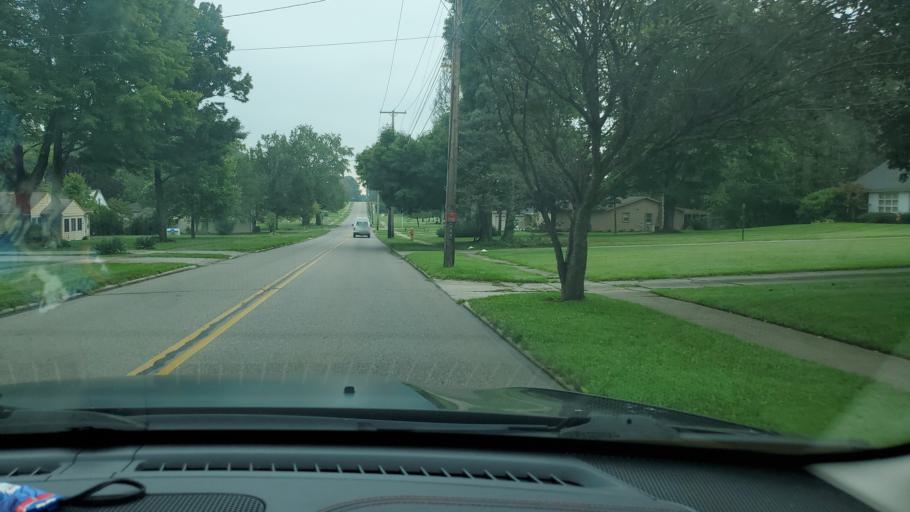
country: US
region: Ohio
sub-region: Mahoning County
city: Boardman
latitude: 41.0463
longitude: -80.6459
